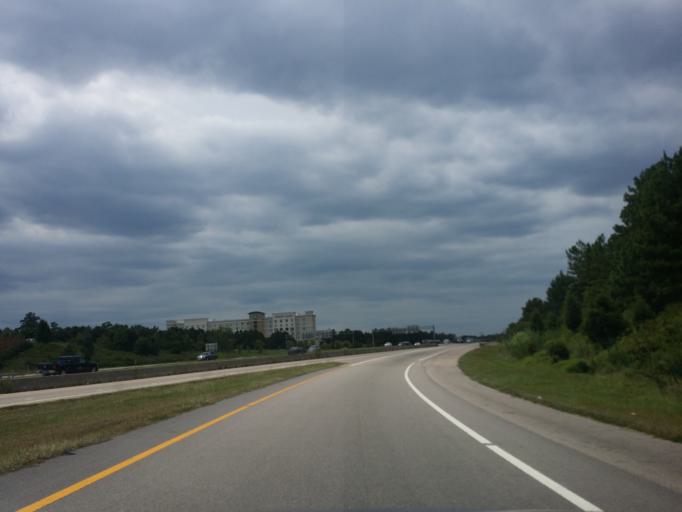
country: US
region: North Carolina
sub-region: Wake County
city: Morrisville
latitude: 35.9064
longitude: -78.7723
